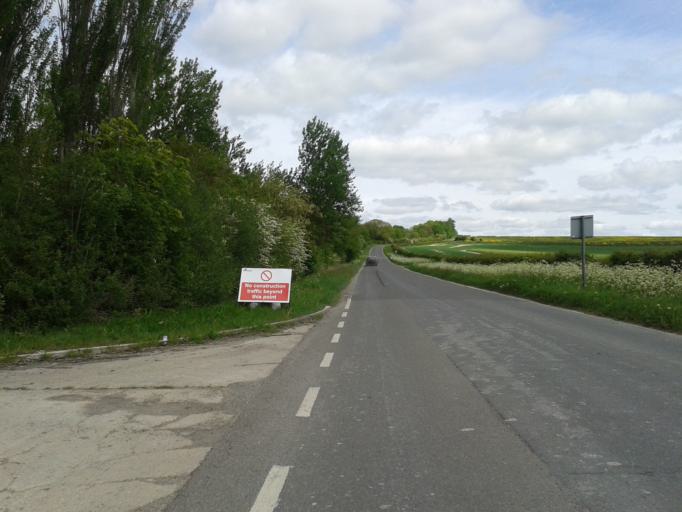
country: GB
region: England
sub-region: Cambridgeshire
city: Haslingfield
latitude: 52.1364
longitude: 0.0411
